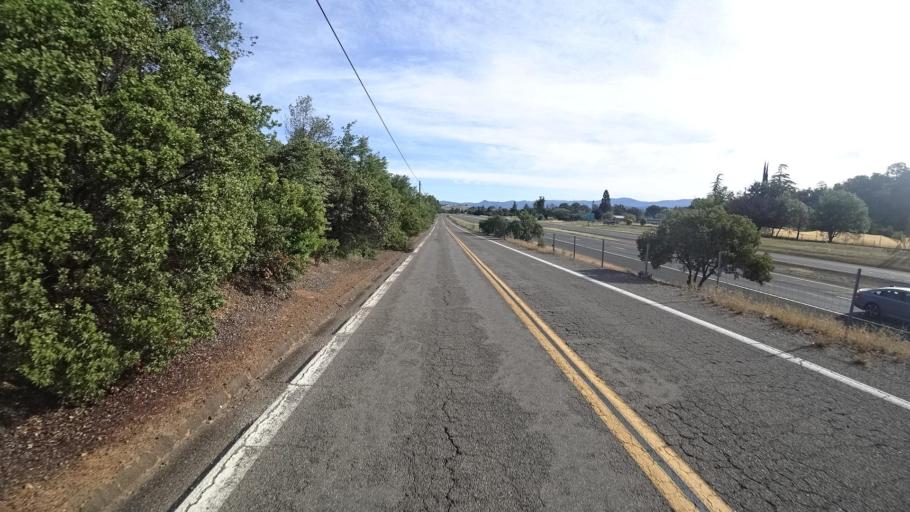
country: US
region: California
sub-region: Lake County
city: Lakeport
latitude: 39.0700
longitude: -122.9318
